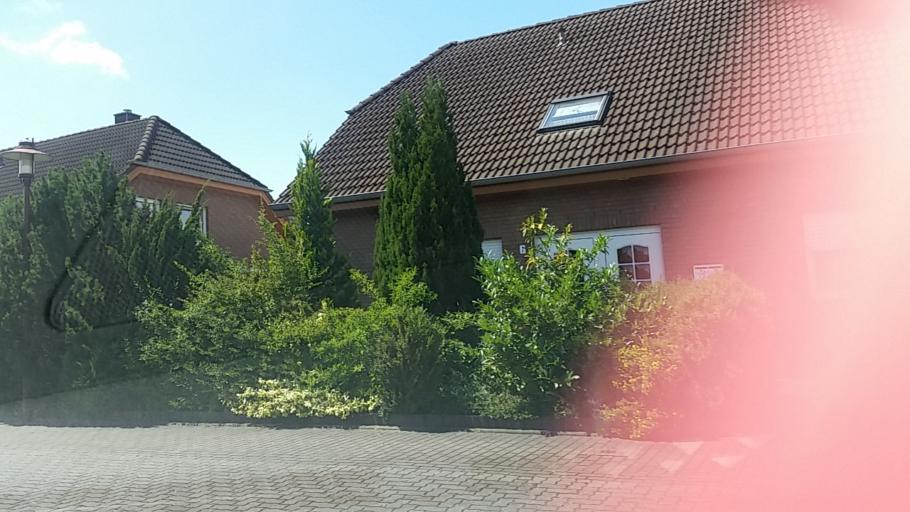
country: DE
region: Lower Saxony
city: Wolfsburg
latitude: 52.4130
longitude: 10.8330
